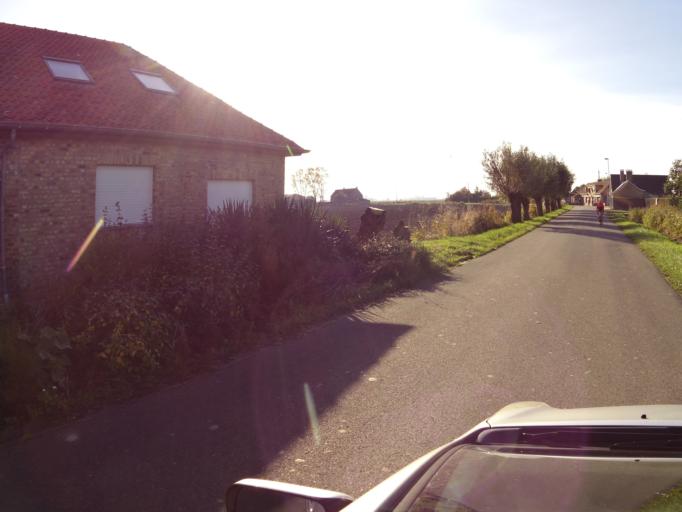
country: BE
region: Flanders
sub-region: Provincie West-Vlaanderen
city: Nieuwpoort
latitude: 51.0893
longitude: 2.7357
